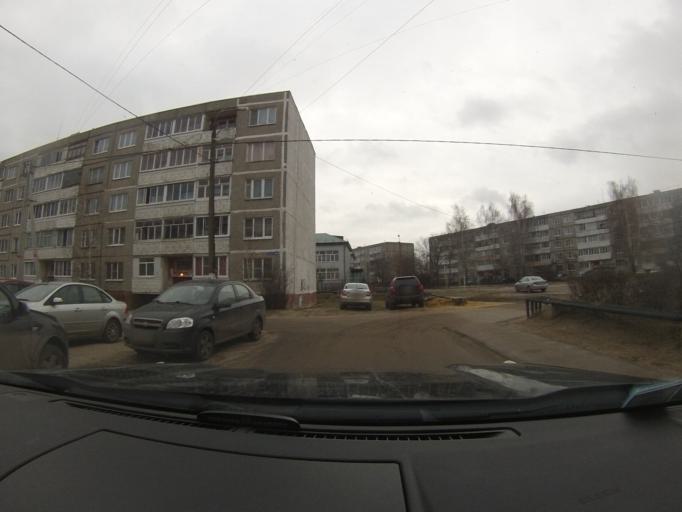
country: RU
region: Moskovskaya
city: Lopatinskiy
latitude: 55.3231
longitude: 38.7011
